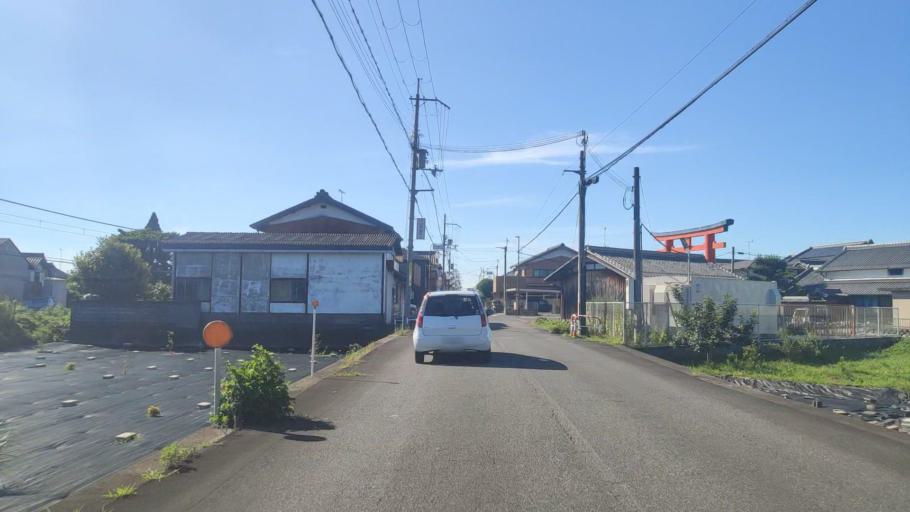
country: JP
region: Shiga Prefecture
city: Minakuchicho-matoba
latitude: 34.8868
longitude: 136.2322
